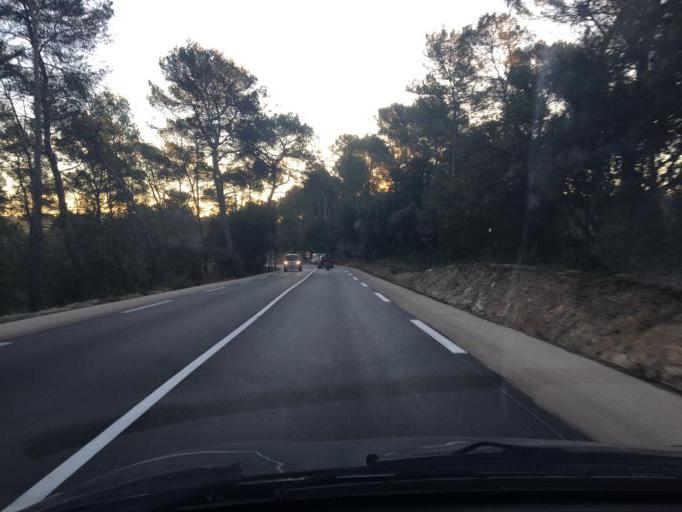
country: FR
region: Provence-Alpes-Cote d'Azur
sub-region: Departement du Var
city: Taradeau
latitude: 43.4612
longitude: 6.4070
